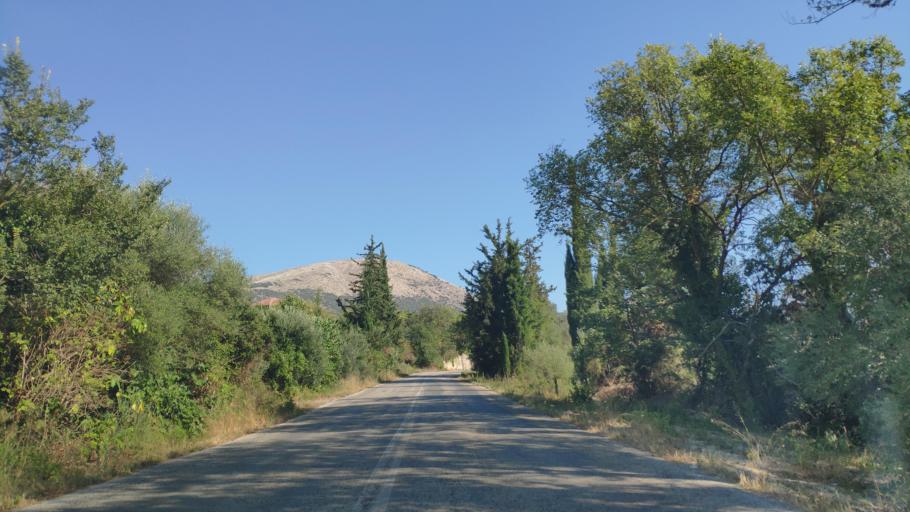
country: GR
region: Epirus
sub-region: Nomos Prevezis
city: Kanalaki
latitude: 39.2653
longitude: 20.6029
